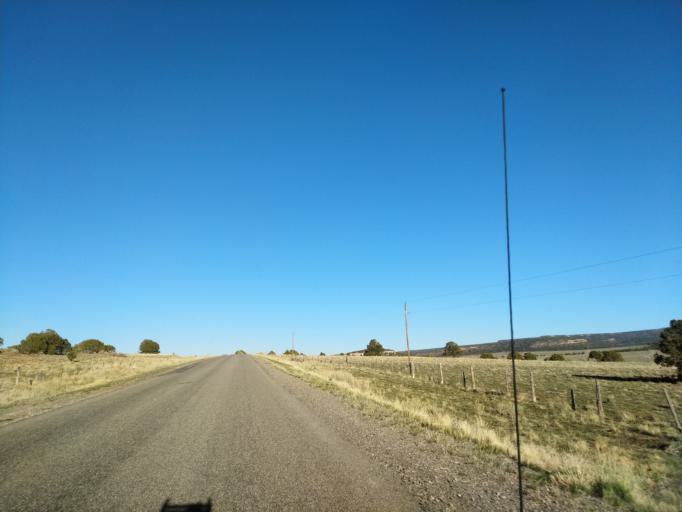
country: US
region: Colorado
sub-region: Mesa County
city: Loma
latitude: 38.9487
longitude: -108.9648
